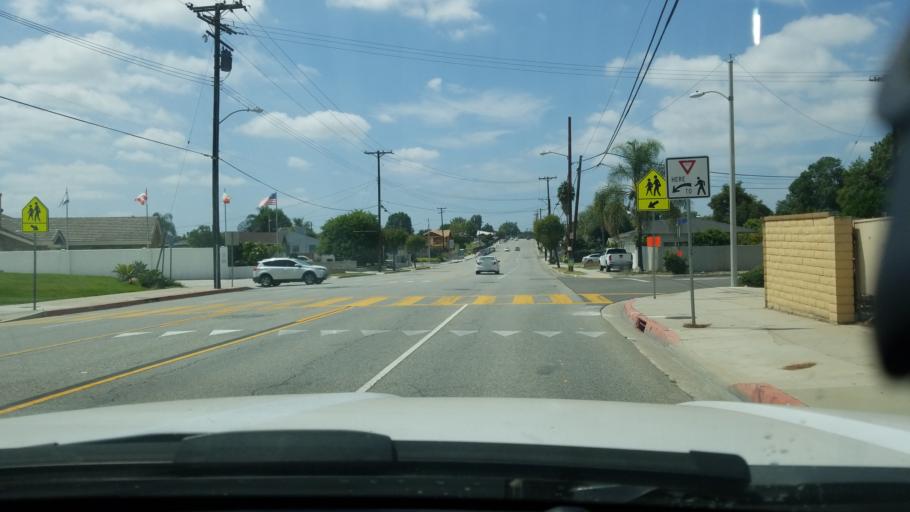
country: US
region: California
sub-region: Los Angeles County
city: South Whittier
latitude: 33.9400
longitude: -118.0342
